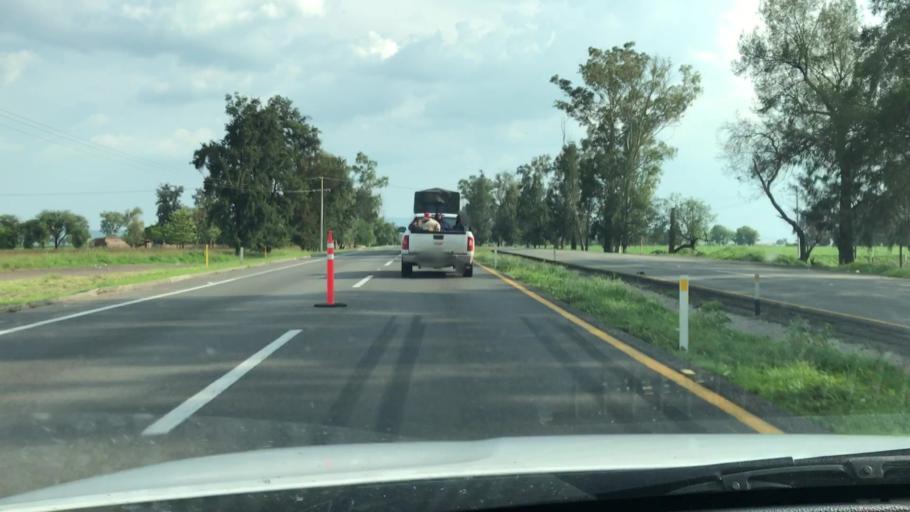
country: MX
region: Guanajuato
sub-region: Irapuato
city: San Ignacio de Rivera (Ojo de Agua)
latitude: 20.5231
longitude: -101.4630
